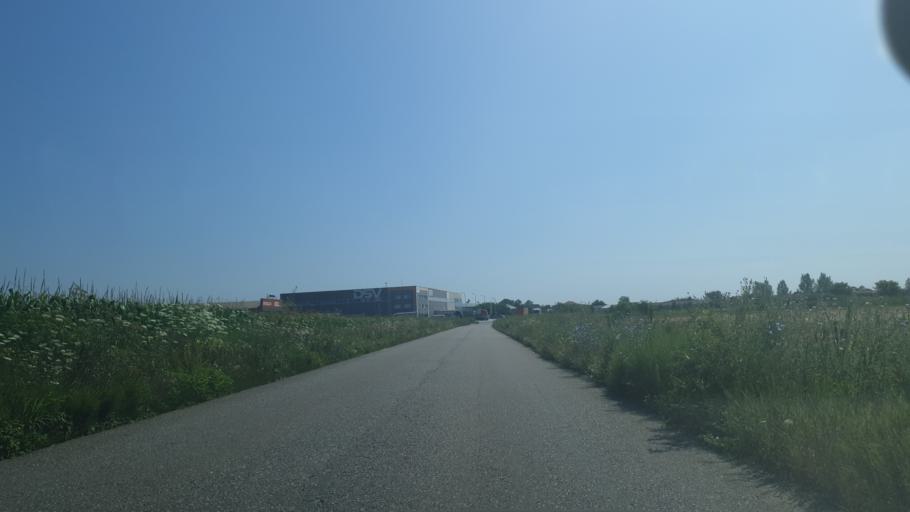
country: RS
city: Simanovci
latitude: 44.8812
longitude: 20.1252
